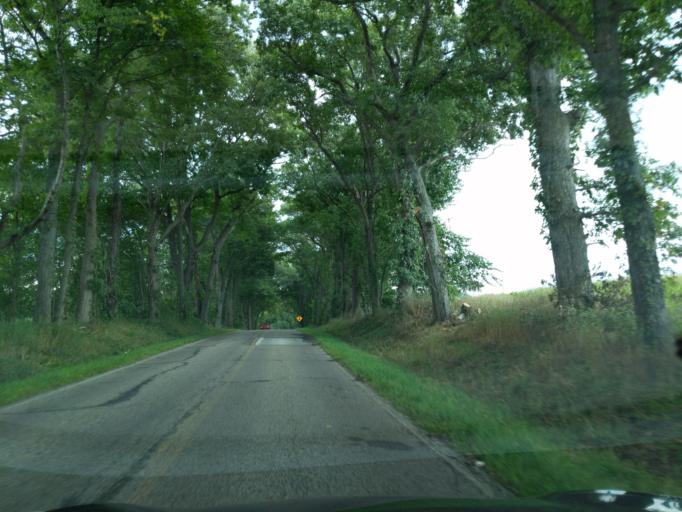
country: US
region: Michigan
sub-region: Eaton County
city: Eaton Rapids
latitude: 42.3786
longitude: -84.6046
